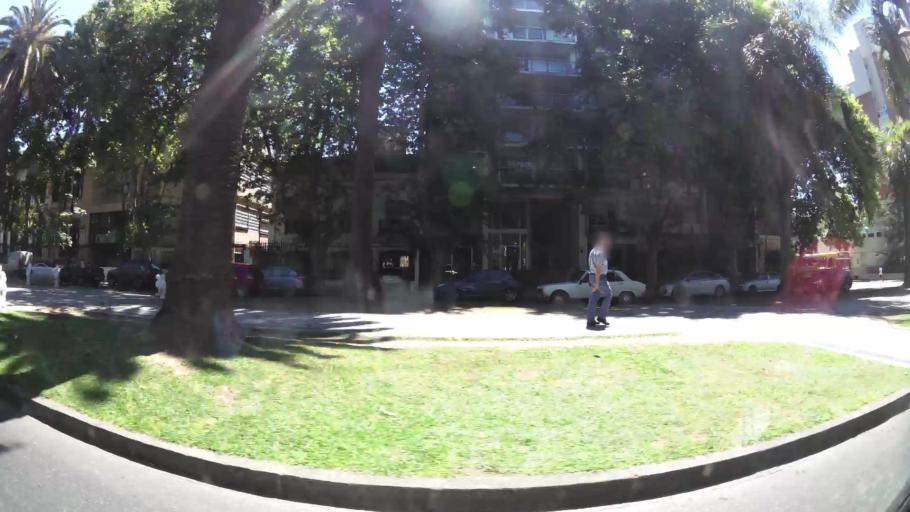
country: AR
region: Santa Fe
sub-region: Departamento de Rosario
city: Rosario
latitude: -32.9417
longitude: -60.6528
